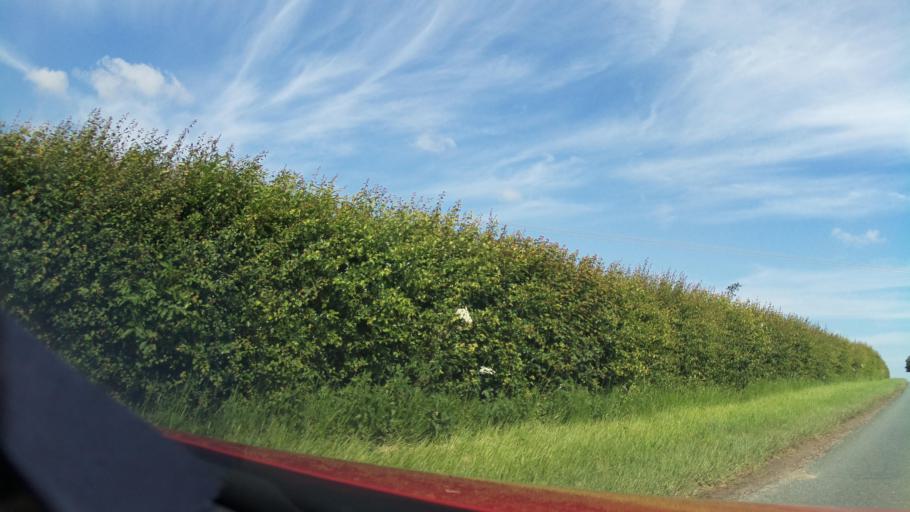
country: GB
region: England
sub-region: Lincolnshire
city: Skellingthorpe
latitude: 53.1607
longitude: -0.6380
